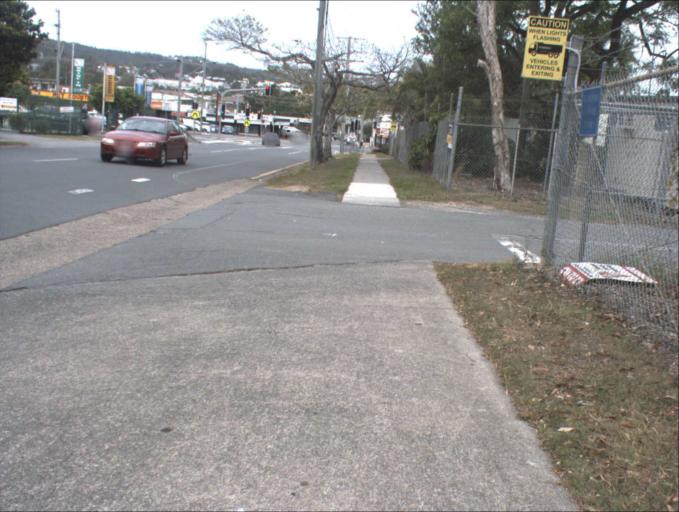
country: AU
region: Queensland
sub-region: Logan
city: Logan City
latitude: -27.6302
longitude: 153.1175
